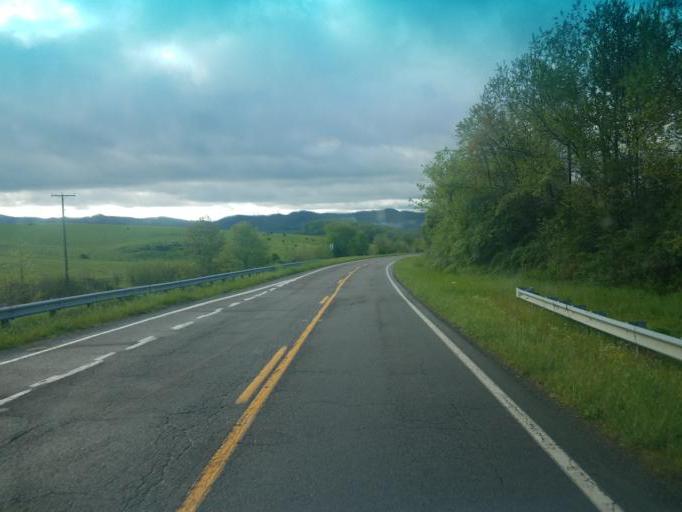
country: US
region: Virginia
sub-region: Washington County
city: Emory
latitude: 36.6770
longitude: -81.8099
